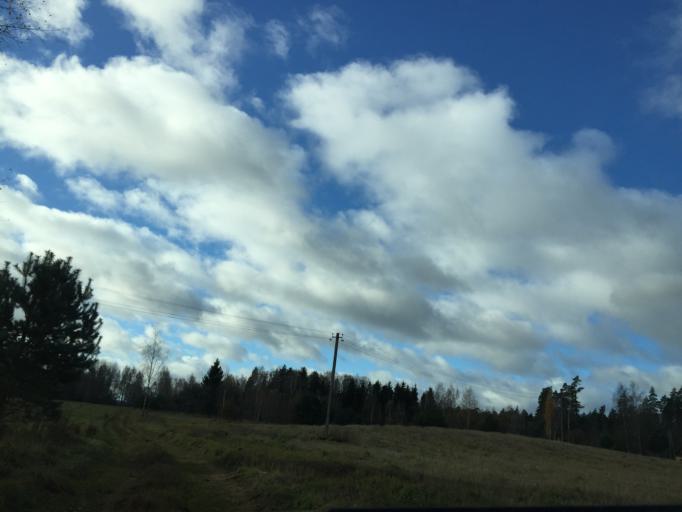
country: LV
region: Engure
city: Smarde
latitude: 56.9680
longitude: 23.2616
